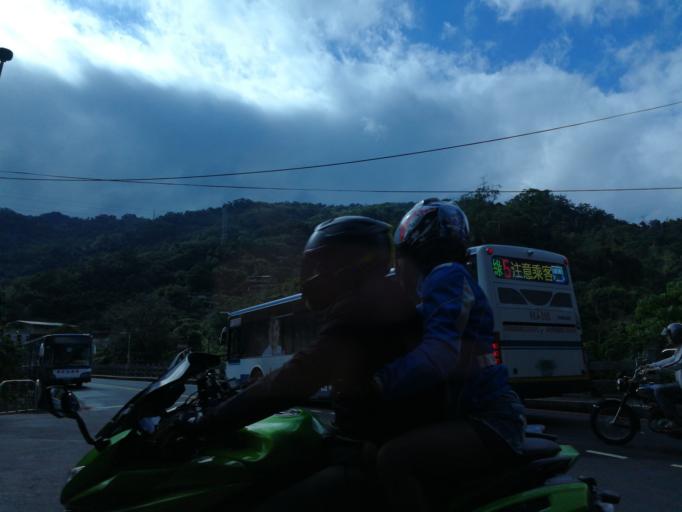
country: TW
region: Taipei
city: Taipei
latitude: 24.9534
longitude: 121.5643
